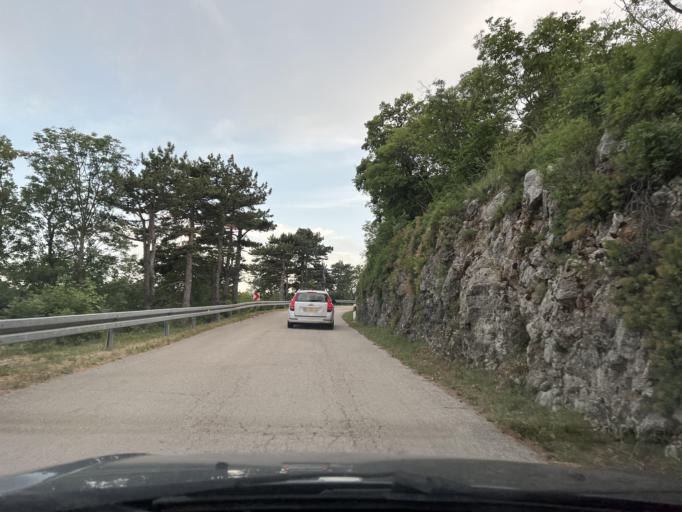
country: HR
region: Primorsko-Goranska
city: Marcelji
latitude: 45.3907
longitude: 14.4190
